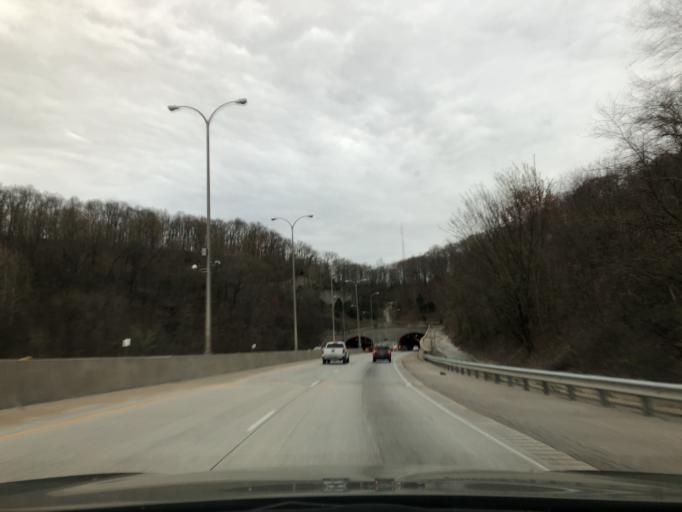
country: US
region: Arkansas
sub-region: Washington County
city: West Fork
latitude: 35.7723
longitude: -94.1868
